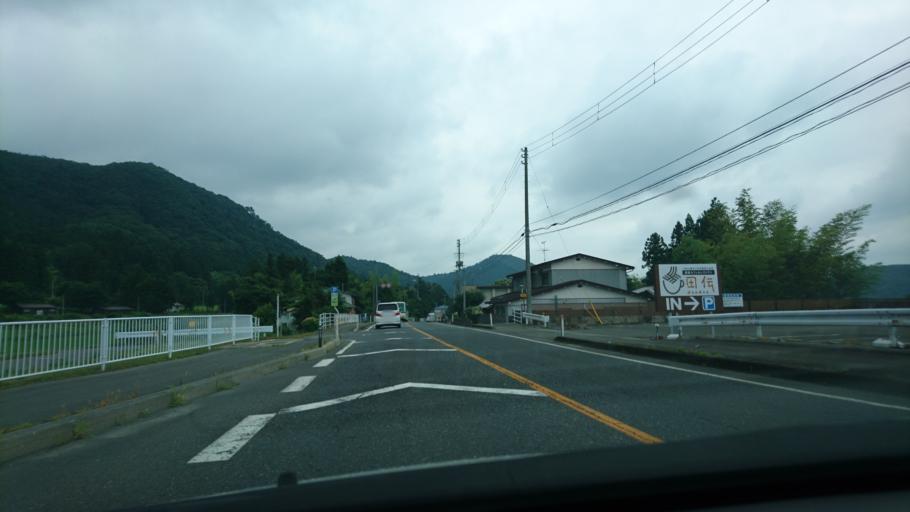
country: JP
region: Miyagi
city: Furukawa
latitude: 38.7322
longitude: 140.7899
